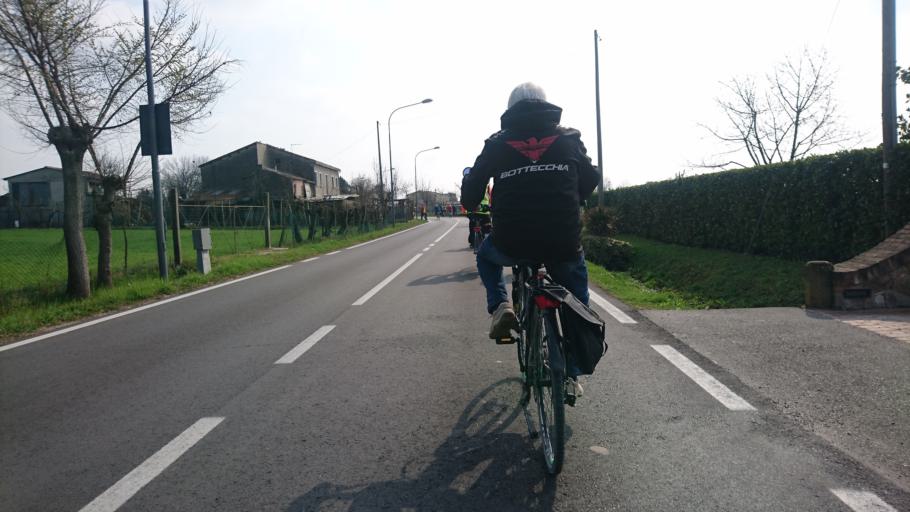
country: IT
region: Veneto
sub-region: Provincia di Padova
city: Abano Terme
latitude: 45.3623
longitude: 11.7622
